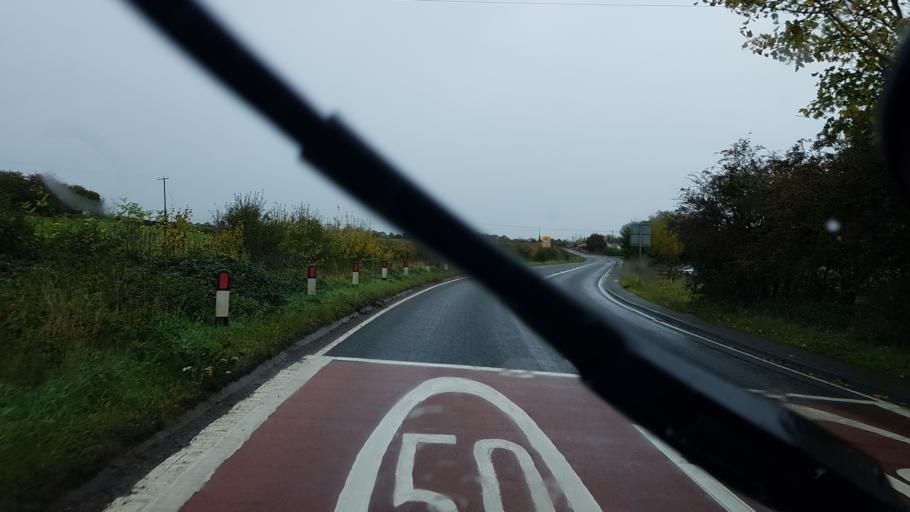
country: GB
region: England
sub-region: Worcestershire
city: Upton upon Severn
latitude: 52.0649
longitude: -2.1955
